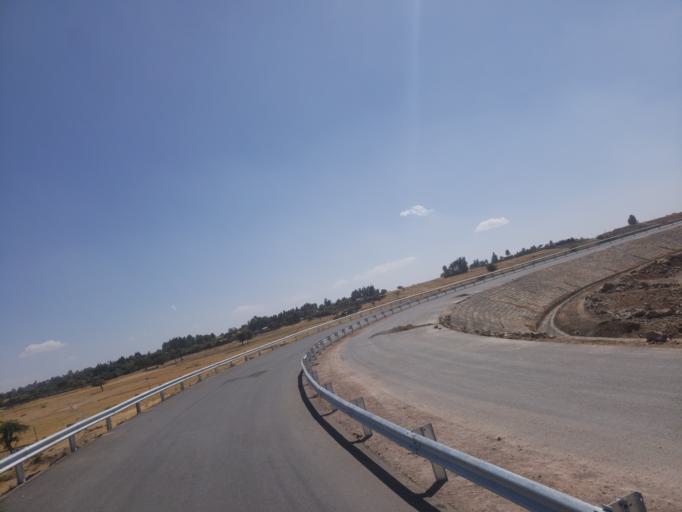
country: ET
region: Oromiya
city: Mojo
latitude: 8.5818
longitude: 39.1729
